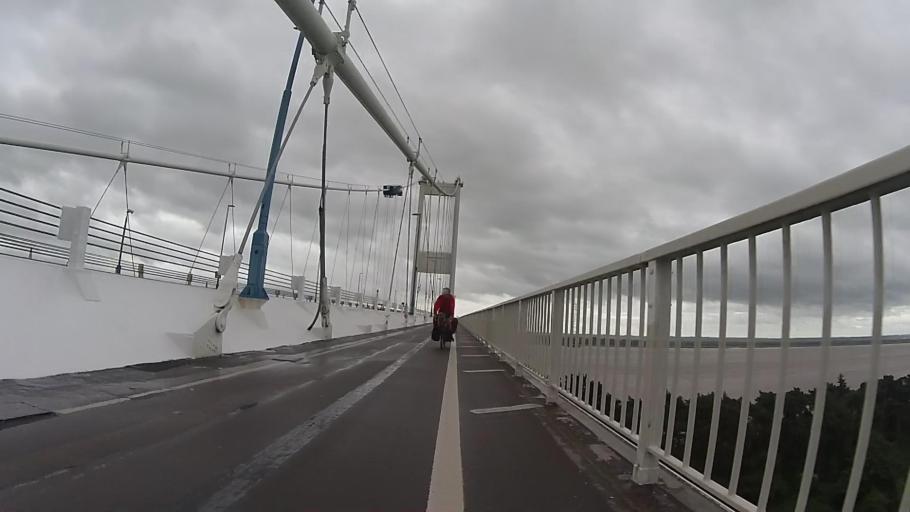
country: GB
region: Wales
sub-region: Monmouthshire
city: Chepstow
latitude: 51.6133
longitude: -2.6494
